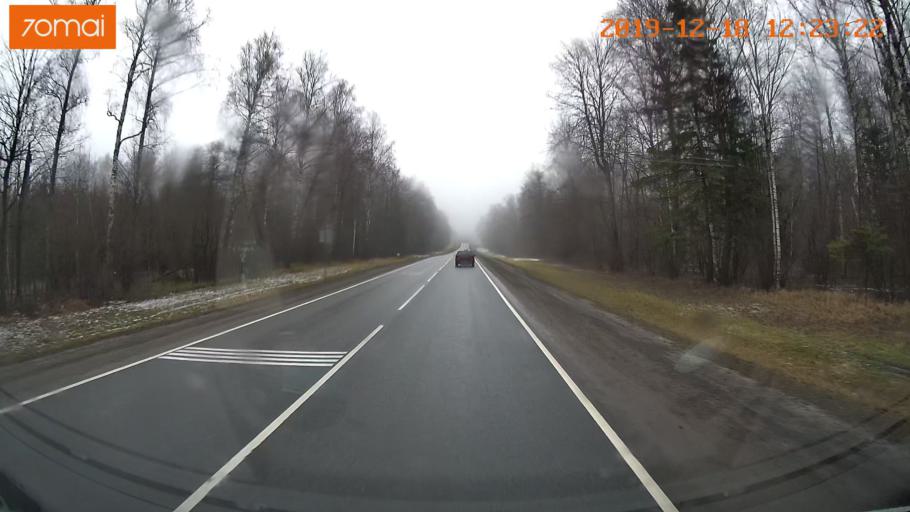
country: RU
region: Moskovskaya
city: Novopetrovskoye
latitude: 56.0128
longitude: 36.4921
